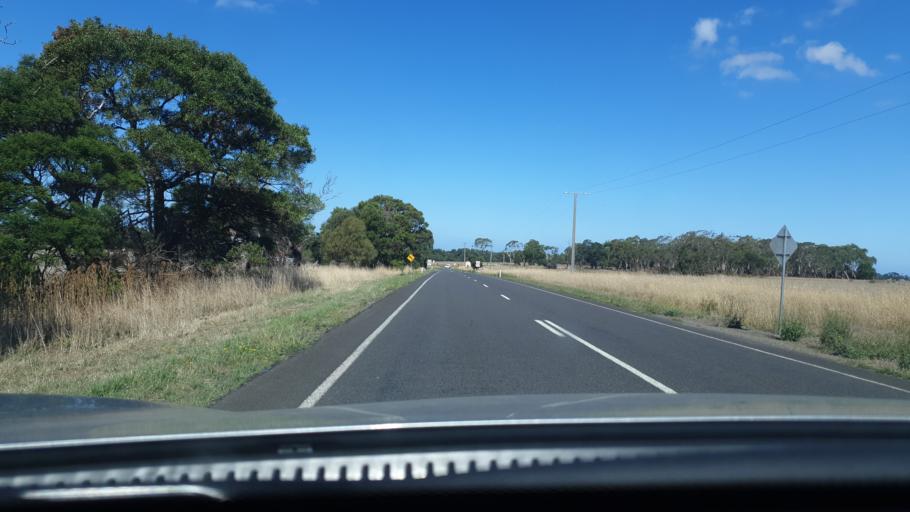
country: AU
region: Victoria
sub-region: Warrnambool
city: Warrnambool
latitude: -38.1810
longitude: 142.4242
